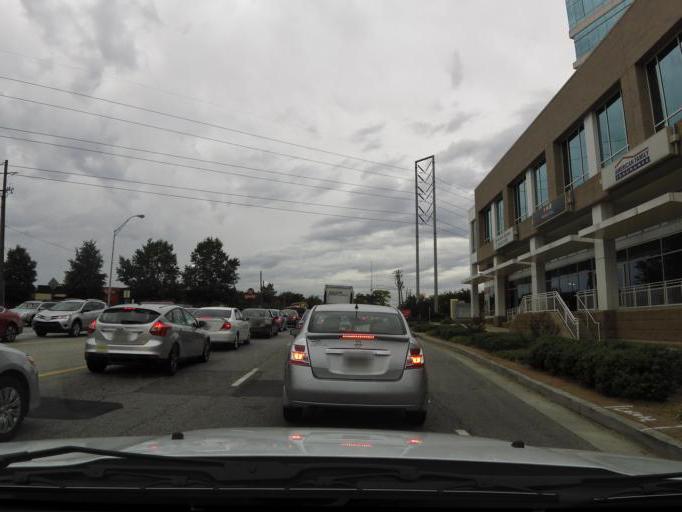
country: US
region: Georgia
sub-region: Fulton County
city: Atlanta
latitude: 33.8047
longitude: -84.4137
